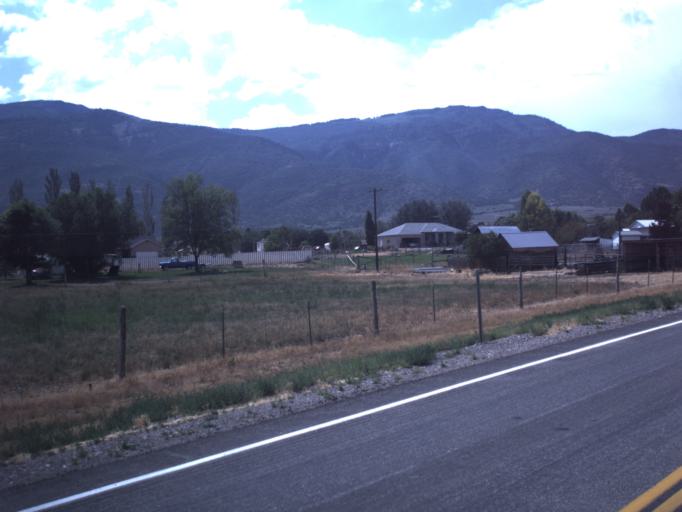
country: US
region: Utah
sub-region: Sanpete County
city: Fountain Green
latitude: 39.6216
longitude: -111.6334
